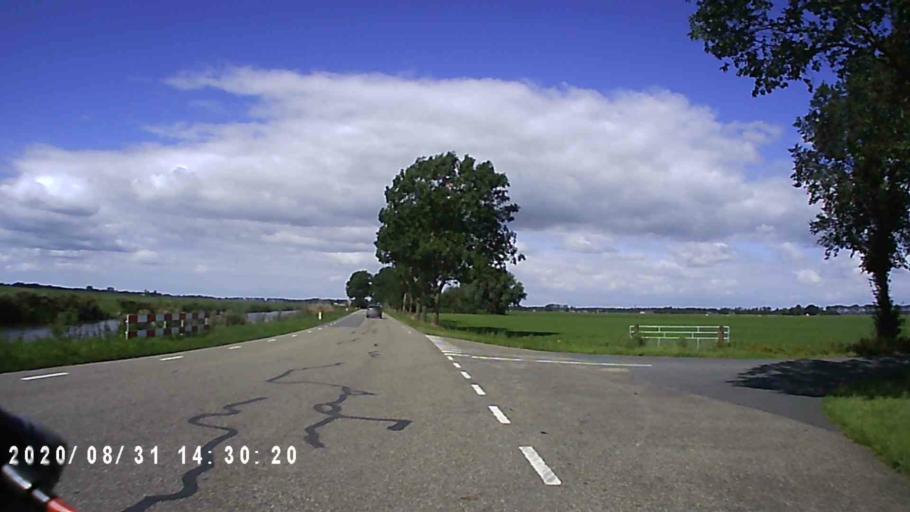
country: NL
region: Groningen
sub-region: Gemeente Zuidhorn
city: Zuidhorn
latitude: 53.2206
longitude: 6.4074
